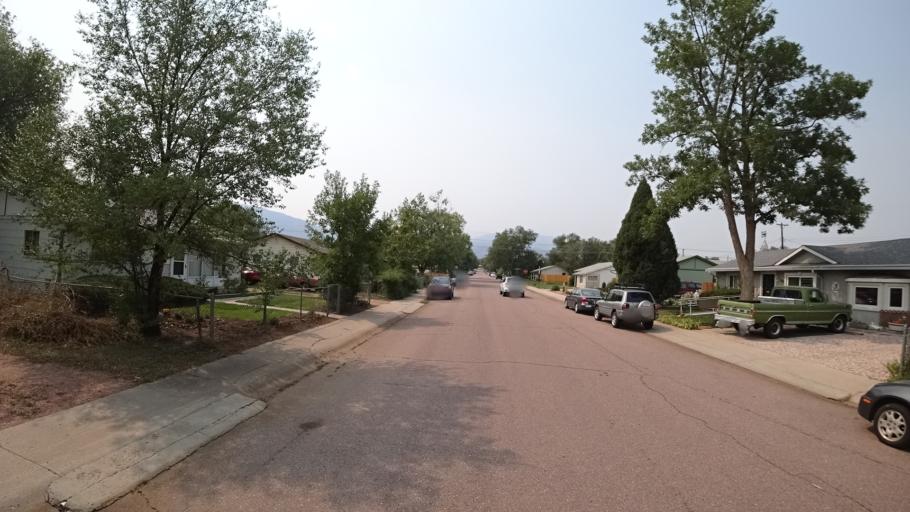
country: US
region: Colorado
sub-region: El Paso County
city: Stratmoor
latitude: 38.7975
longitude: -104.8026
